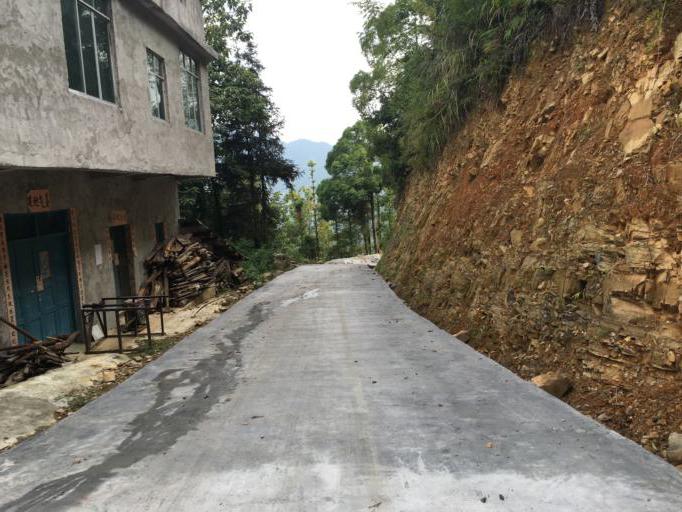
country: CN
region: Guangxi Zhuangzu Zizhiqu
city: Tongle
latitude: 25.2986
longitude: 106.1637
